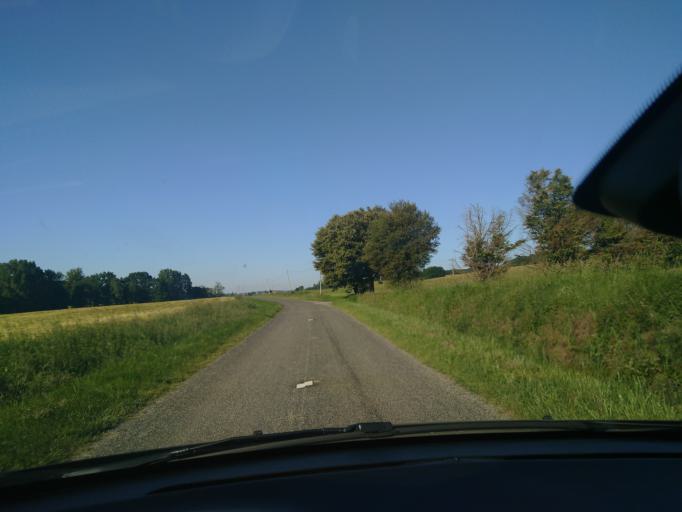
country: FR
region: Midi-Pyrenees
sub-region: Departement du Tarn-et-Garonne
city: Beaumont-de-Lomagne
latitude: 43.8338
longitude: 1.0670
